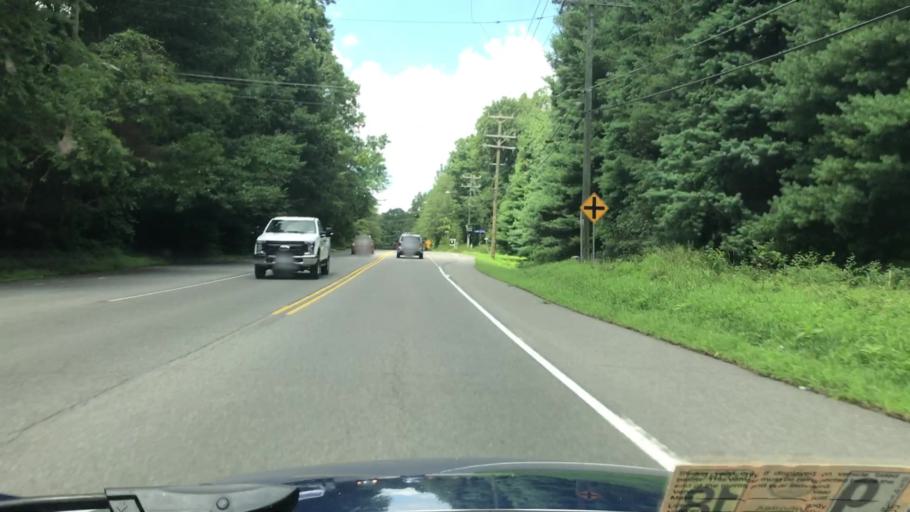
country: US
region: Virginia
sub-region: Fairfax County
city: Wolf Trap
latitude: 38.9258
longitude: -77.3197
